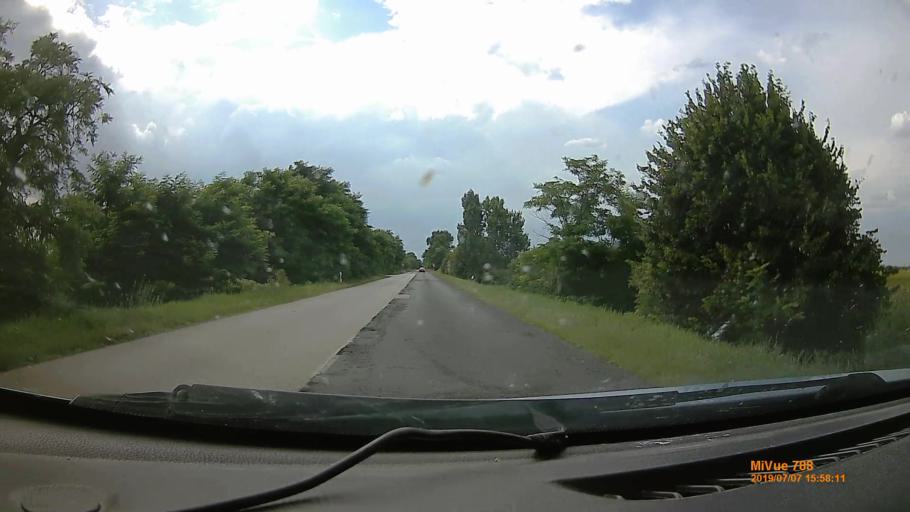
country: HU
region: Pest
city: Szentlorinckata
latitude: 47.5800
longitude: 19.7537
